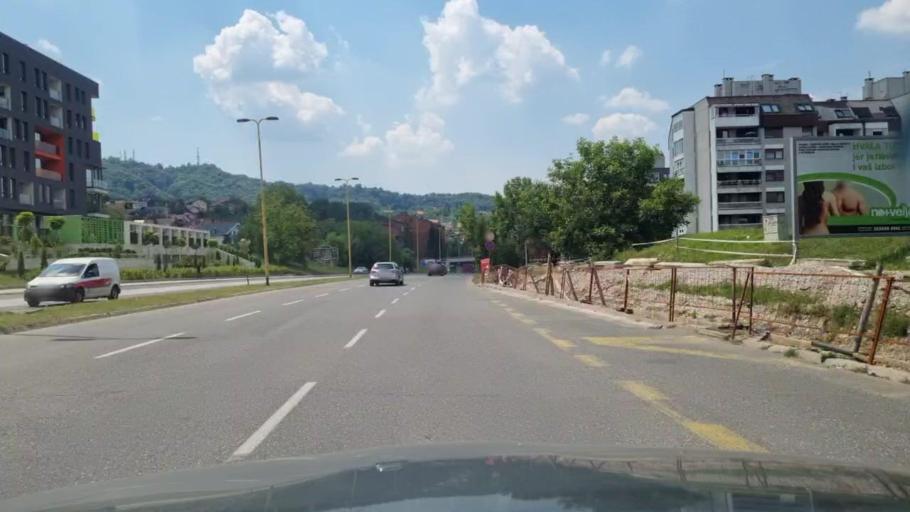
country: BA
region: Federation of Bosnia and Herzegovina
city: Tuzla
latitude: 44.5287
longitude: 18.6943
